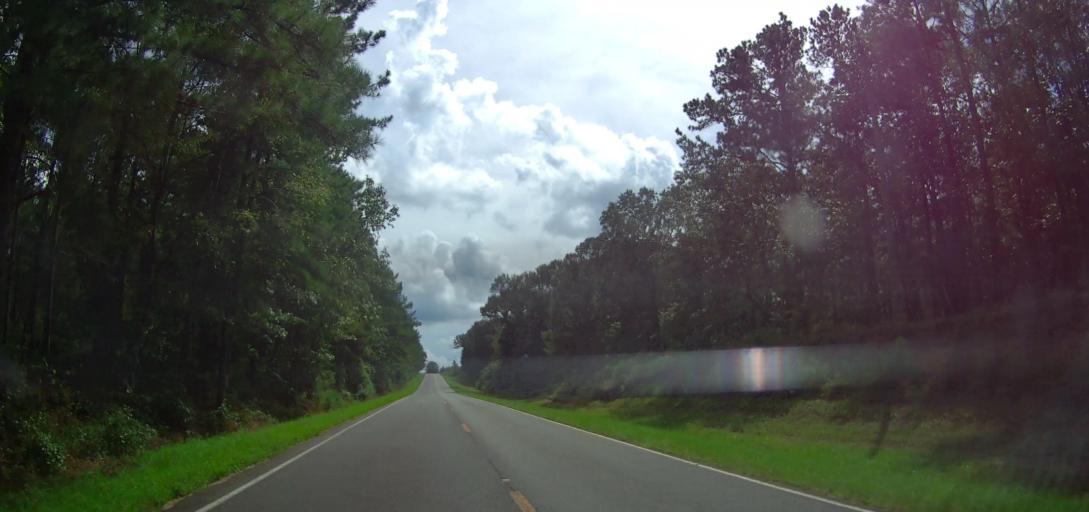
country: US
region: Georgia
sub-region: Taylor County
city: Butler
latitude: 32.4841
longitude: -84.2057
